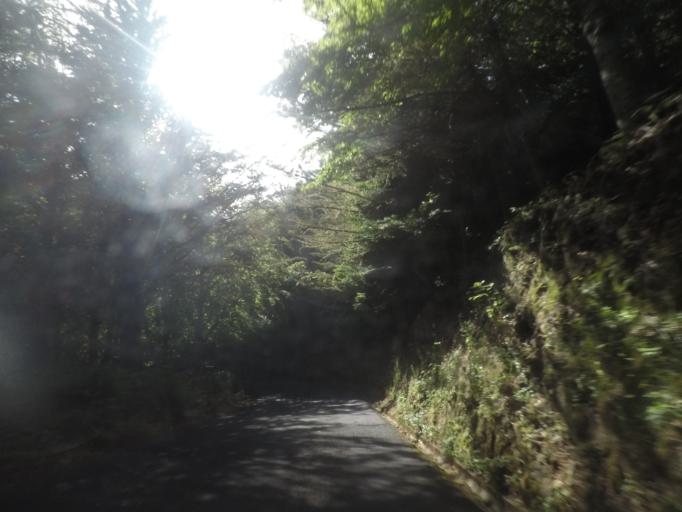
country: PT
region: Madeira
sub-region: Santa Cruz
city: Camacha
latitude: 32.7110
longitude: -16.8782
